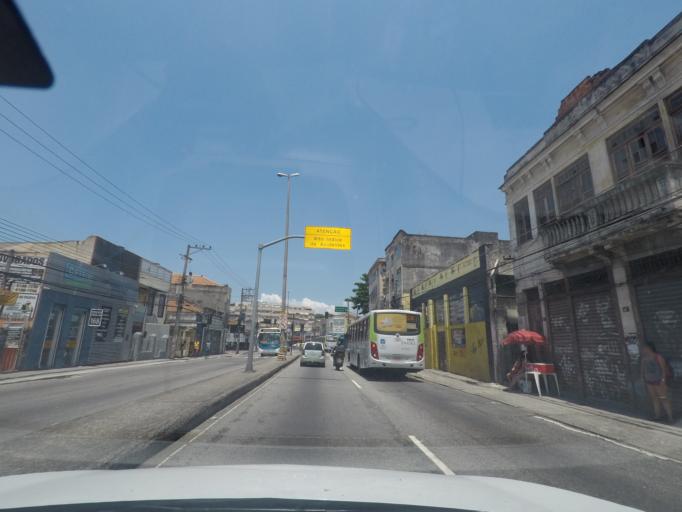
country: BR
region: Rio de Janeiro
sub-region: Rio De Janeiro
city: Rio de Janeiro
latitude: -22.8854
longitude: -43.3002
